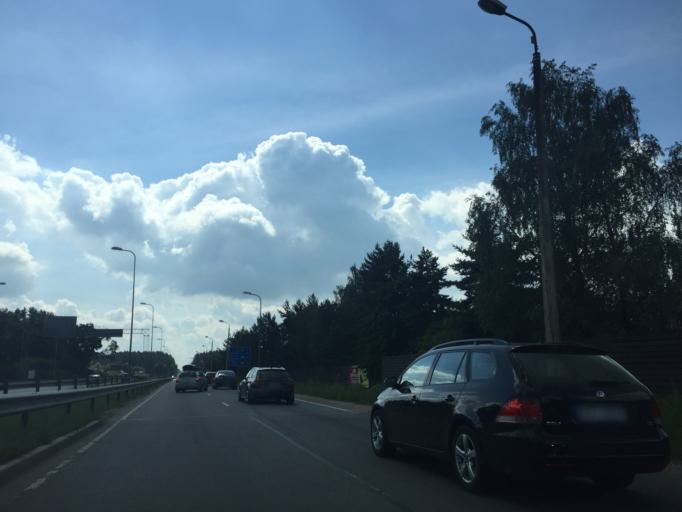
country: LV
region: Kekava
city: Balozi
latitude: 56.8990
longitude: 24.1361
